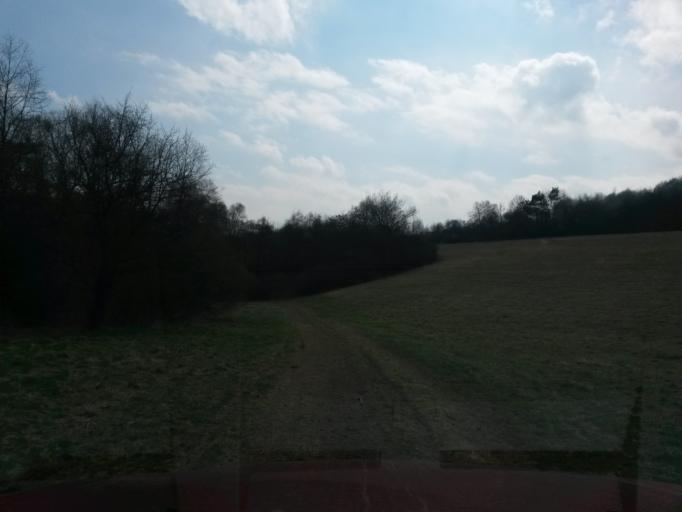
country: SK
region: Presovsky
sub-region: Okres Presov
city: Presov
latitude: 48.9435
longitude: 21.1698
